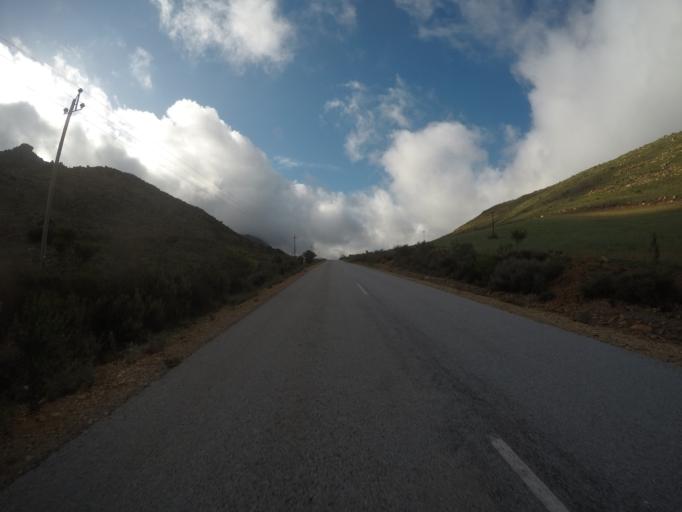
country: ZA
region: Western Cape
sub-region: West Coast District Municipality
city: Clanwilliam
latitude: -32.3695
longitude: 18.8644
